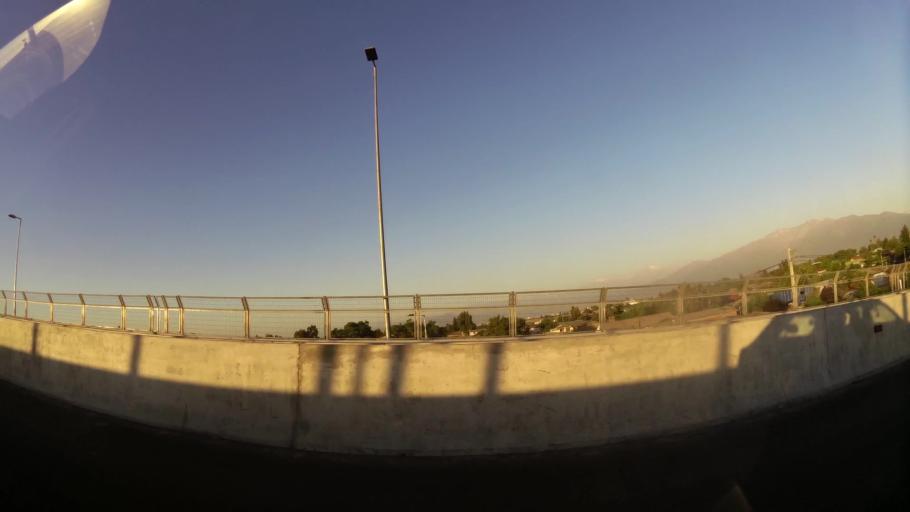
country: CL
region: Santiago Metropolitan
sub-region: Provincia de Maipo
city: San Bernardo
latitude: -33.5745
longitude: -70.6975
